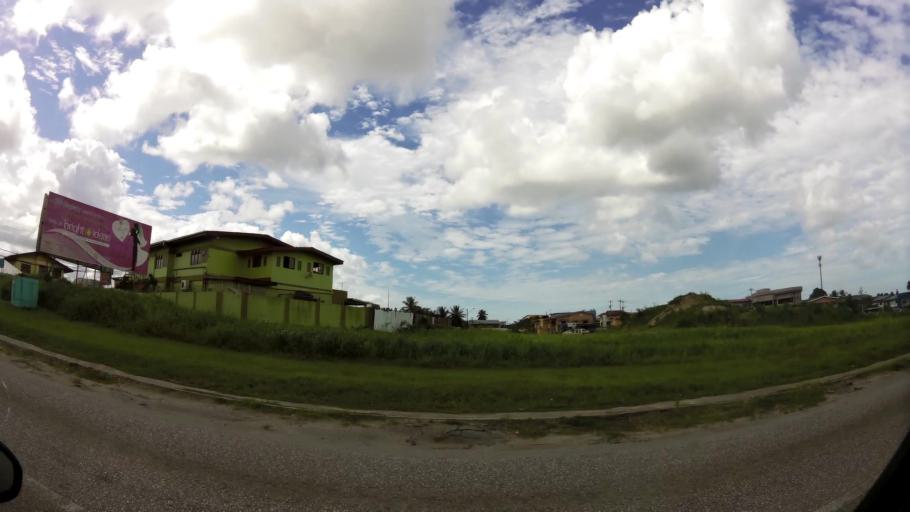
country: TT
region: City of San Fernando
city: Marabella
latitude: 10.2994
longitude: -61.4483
